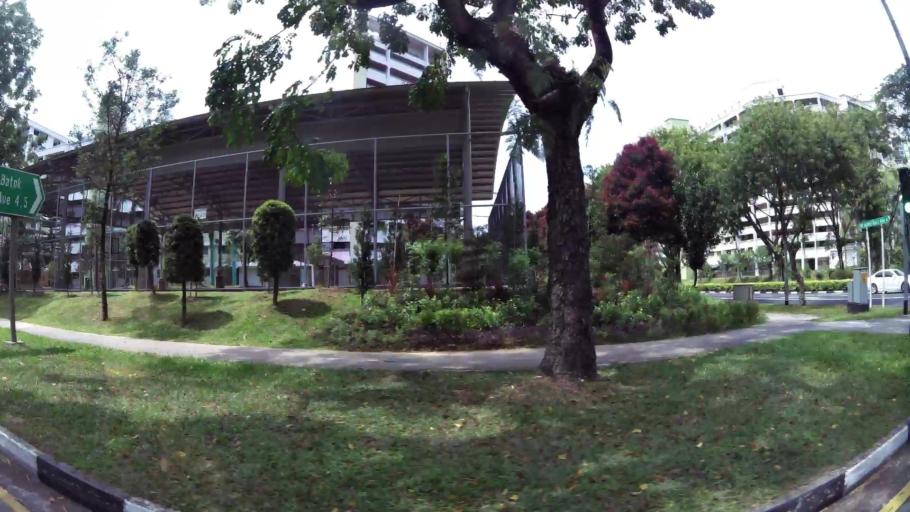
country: SG
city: Singapore
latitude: 1.3496
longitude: 103.7607
